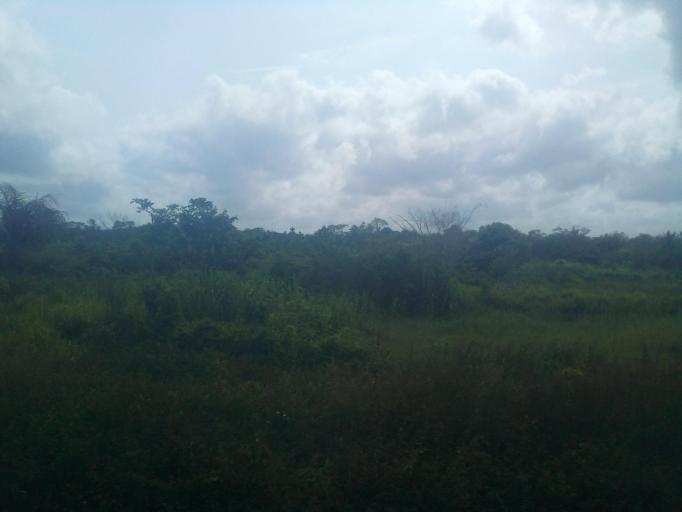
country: BR
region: Maranhao
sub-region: Icatu
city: Icatu
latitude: -2.9397
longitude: -44.3464
